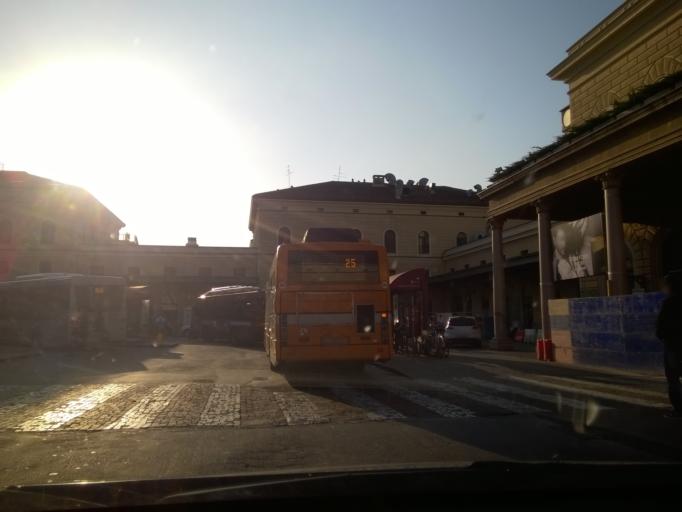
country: IT
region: Emilia-Romagna
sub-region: Provincia di Bologna
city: Bologna
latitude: 44.5057
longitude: 11.3433
